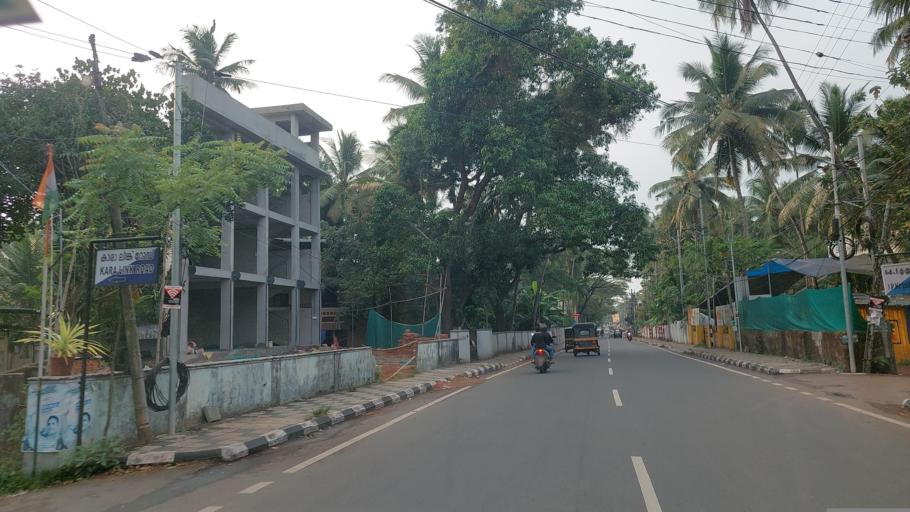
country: IN
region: Kerala
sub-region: Kozhikode
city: Kozhikode
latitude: 11.2879
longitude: 75.7785
